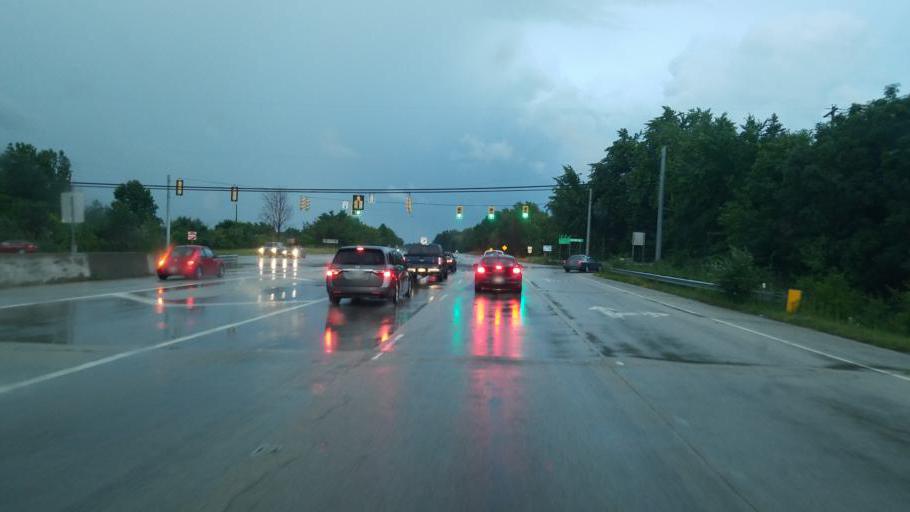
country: US
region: Ohio
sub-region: Wayne County
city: Doylestown
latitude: 40.9892
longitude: -81.6637
